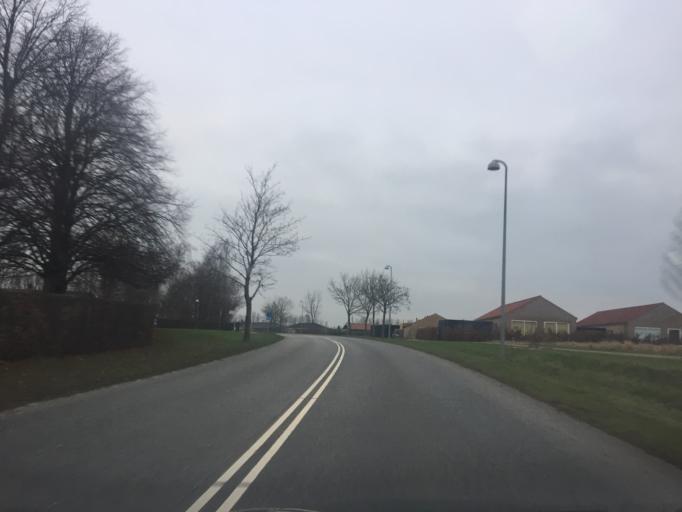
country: DK
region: Zealand
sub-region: Roskilde Kommune
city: Gundsomagle
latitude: 55.7349
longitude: 12.1607
